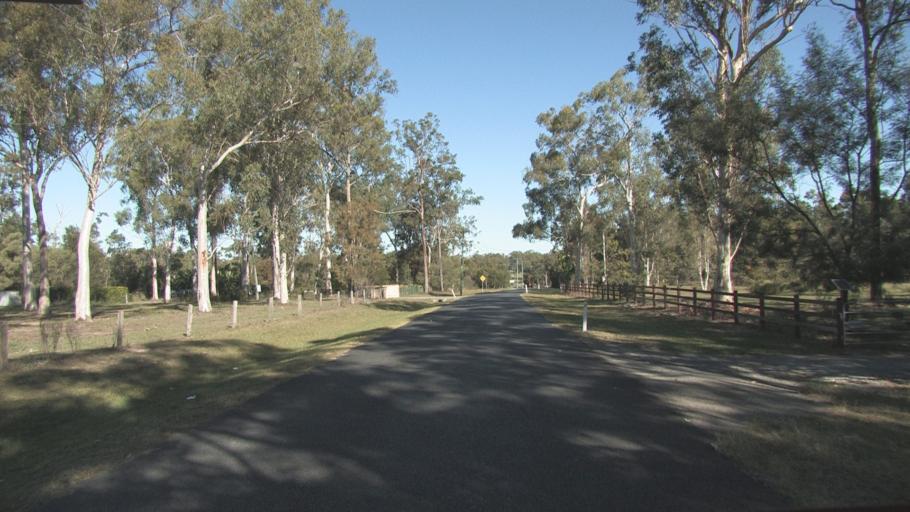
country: AU
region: Queensland
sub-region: Logan
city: Chambers Flat
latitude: -27.7317
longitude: 153.0721
